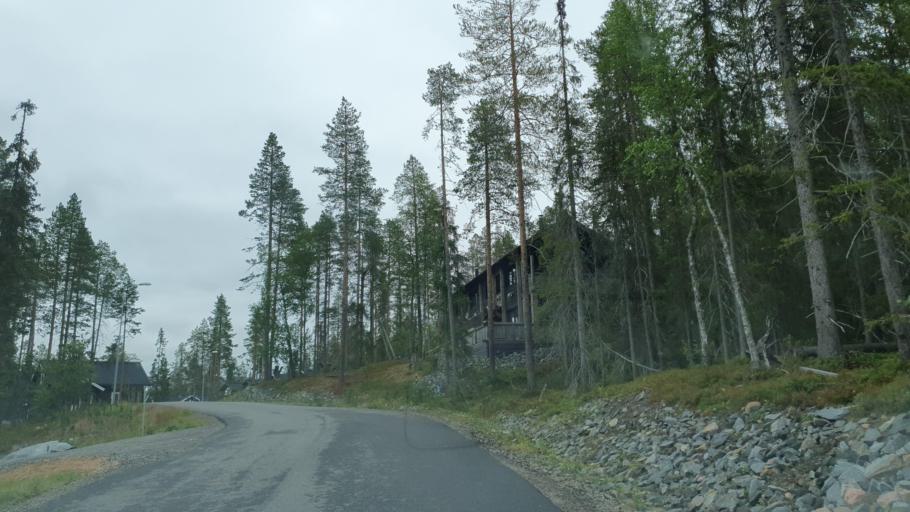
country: FI
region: Lapland
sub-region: Tunturi-Lappi
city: Kolari
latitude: 67.5923
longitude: 24.1750
